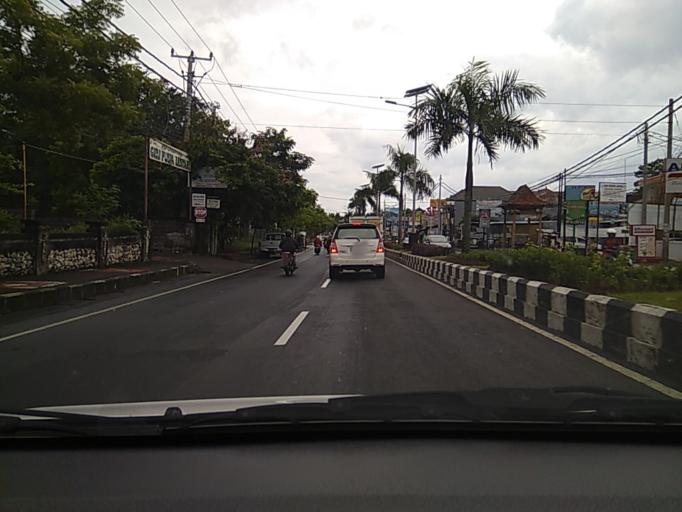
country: ID
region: Bali
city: Bualu
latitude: -8.7849
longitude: 115.1960
